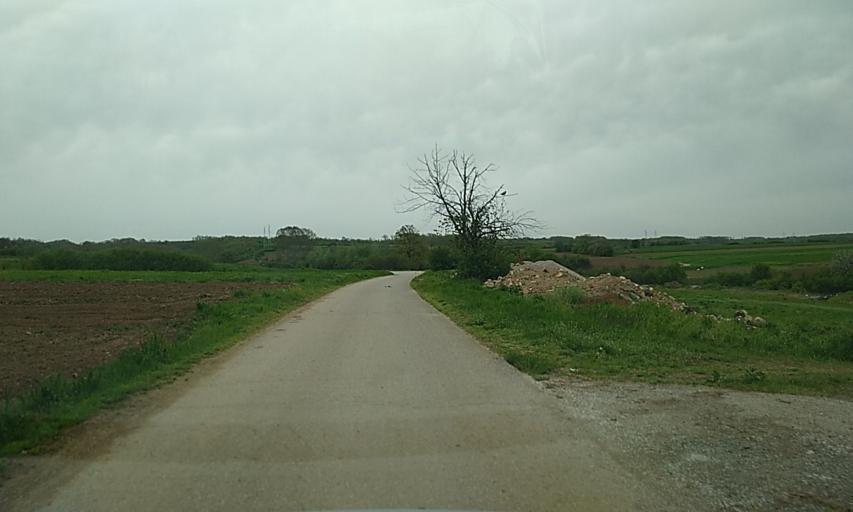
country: RS
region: Central Serbia
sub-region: Nisavski Okrug
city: Razanj
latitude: 43.5699
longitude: 21.5135
